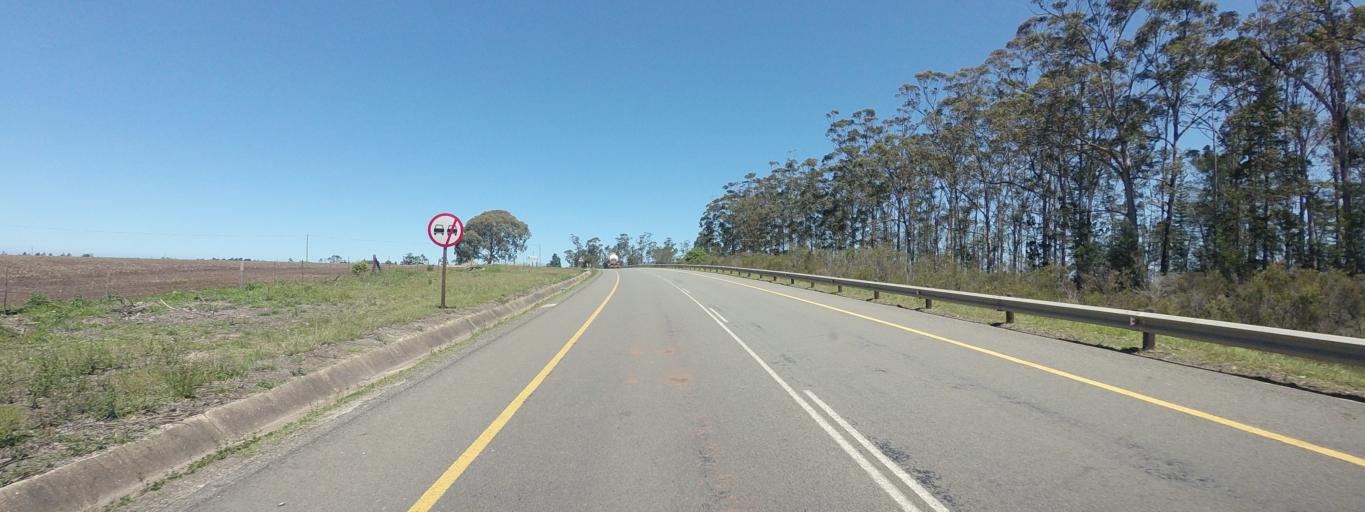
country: ZA
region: Western Cape
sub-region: Eden District Municipality
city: Plettenberg Bay
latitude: -33.9508
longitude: 23.4786
